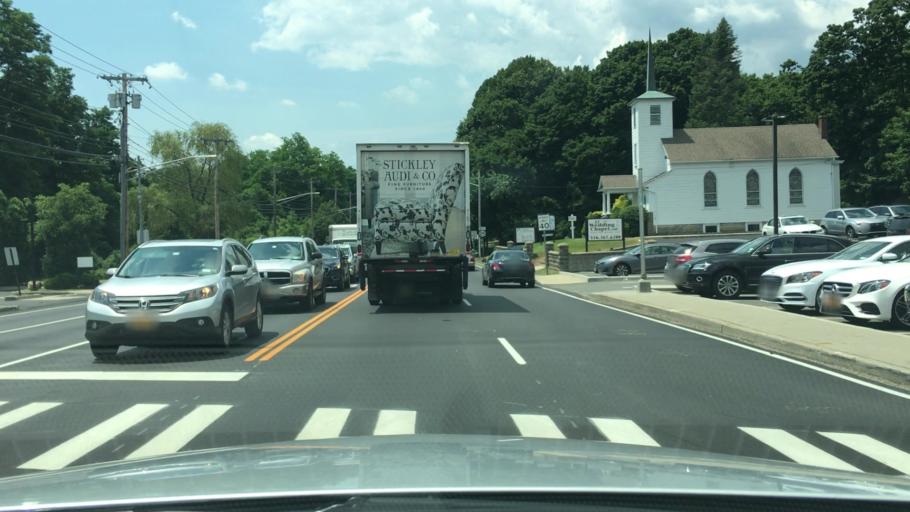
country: US
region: New York
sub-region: Nassau County
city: Woodbury
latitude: 40.8160
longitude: -73.4685
